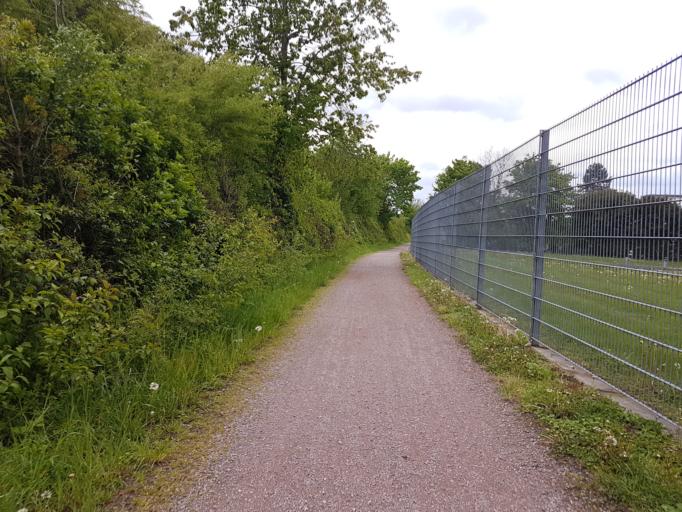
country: CH
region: Aargau
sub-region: Bezirk Zurzach
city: Koblenz
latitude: 47.6225
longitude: 8.2645
